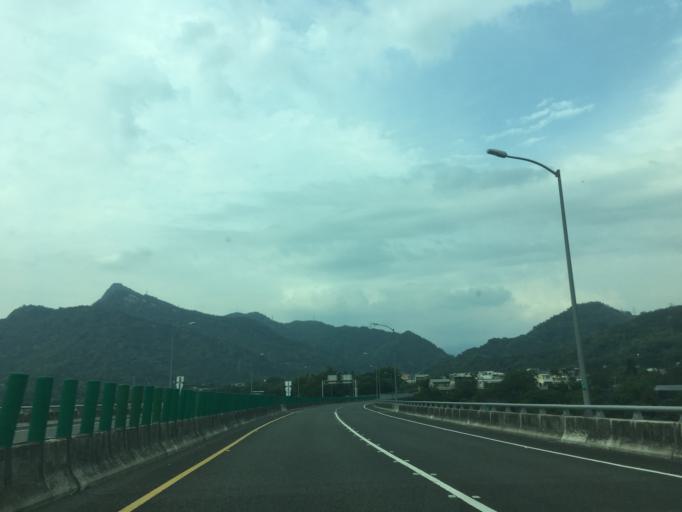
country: TW
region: Taiwan
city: Zhongxing New Village
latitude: 24.0098
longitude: 120.8139
